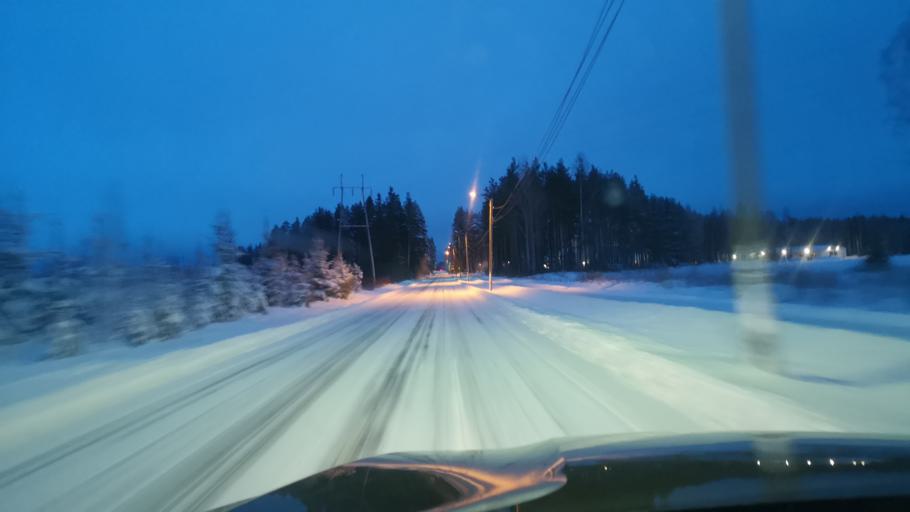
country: FI
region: Varsinais-Suomi
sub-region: Loimaa
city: Loimaa
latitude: 60.8655
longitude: 23.0840
